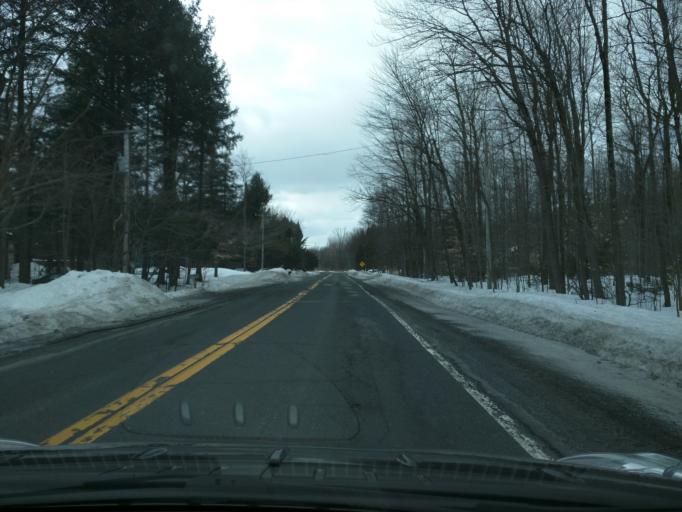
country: CA
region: Quebec
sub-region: Monteregie
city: Sainte-Julie
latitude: 45.6824
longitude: -73.2567
